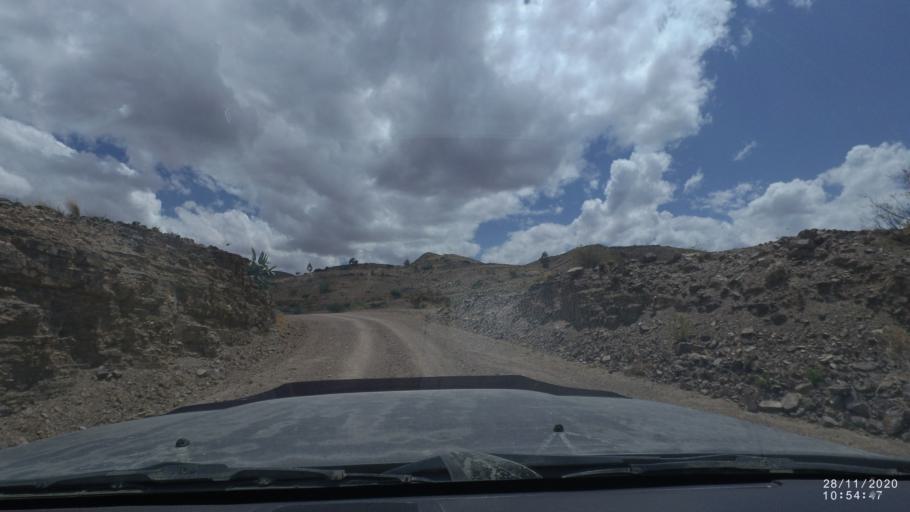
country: BO
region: Cochabamba
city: Capinota
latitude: -17.7764
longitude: -66.1184
